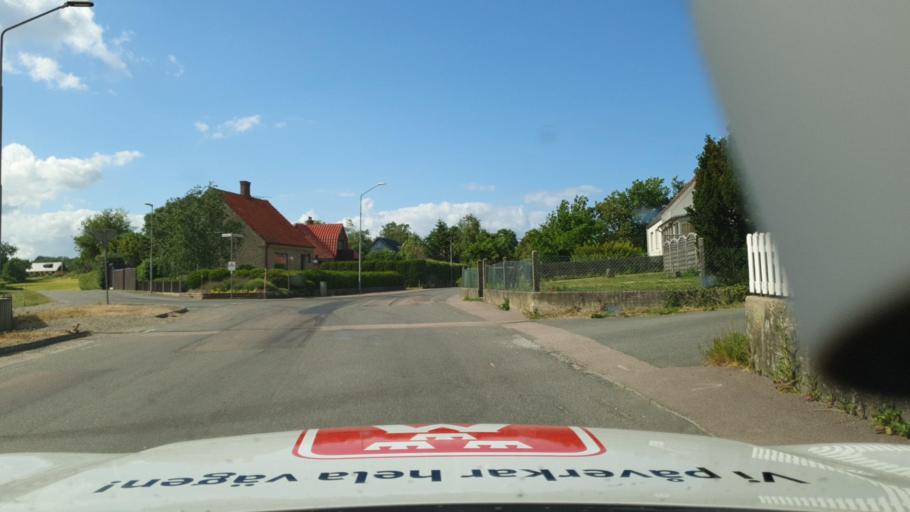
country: SE
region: Skane
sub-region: Simrishamns Kommun
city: Simrishamn
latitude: 55.5553
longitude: 14.3143
